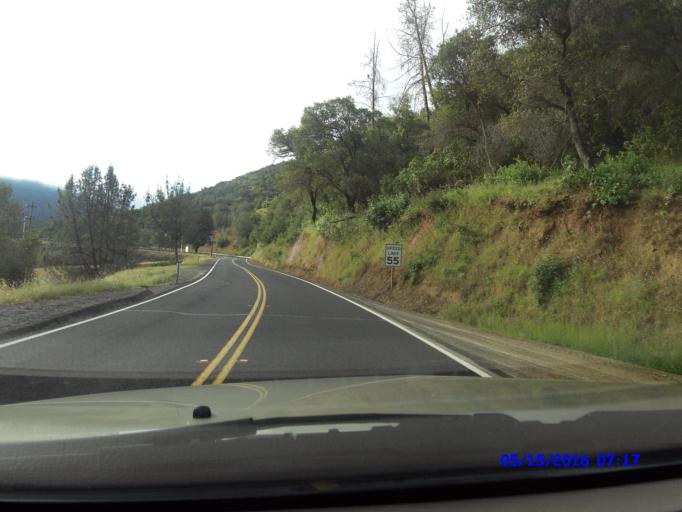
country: US
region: California
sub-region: Tuolumne County
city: Tuolumne City
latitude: 37.8117
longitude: -120.3085
